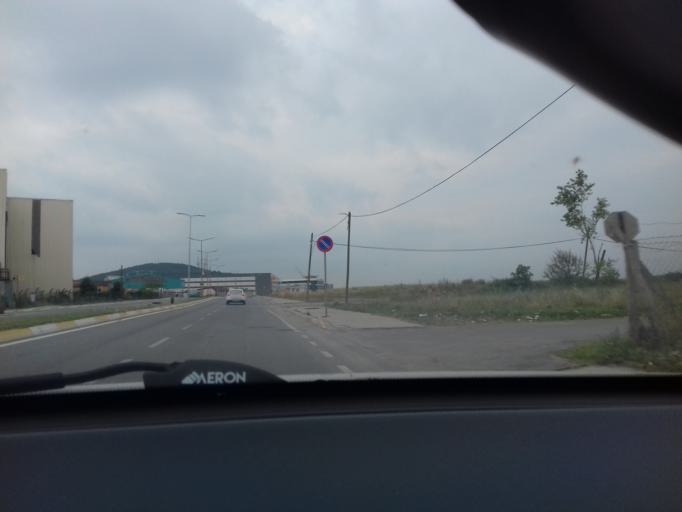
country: TR
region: Istanbul
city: Icmeler
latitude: 40.8888
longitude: 29.3530
